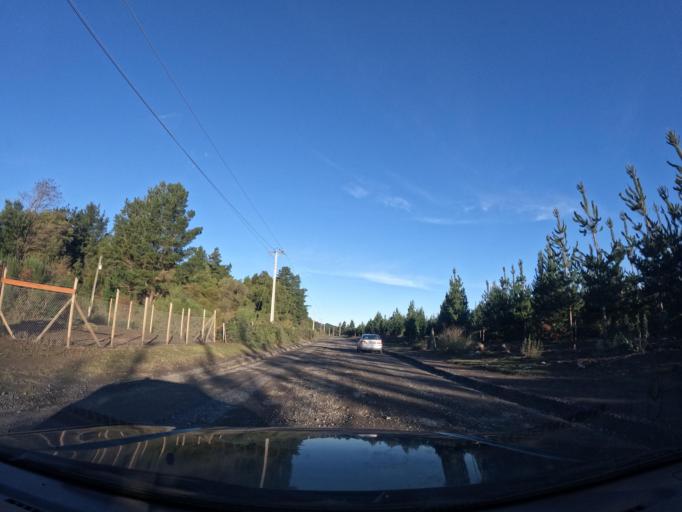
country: CL
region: Biobio
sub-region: Provincia de Concepcion
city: Chiguayante
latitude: -37.0727
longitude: -72.9438
